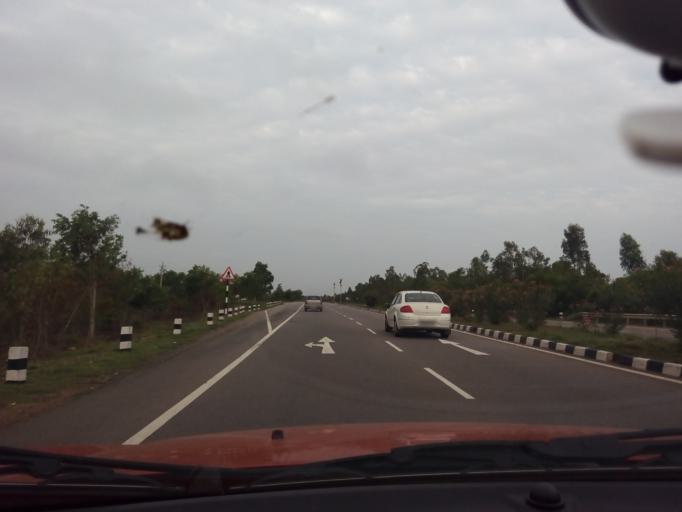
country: IN
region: Karnataka
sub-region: Mandya
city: Belluru
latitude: 12.9797
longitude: 76.8369
